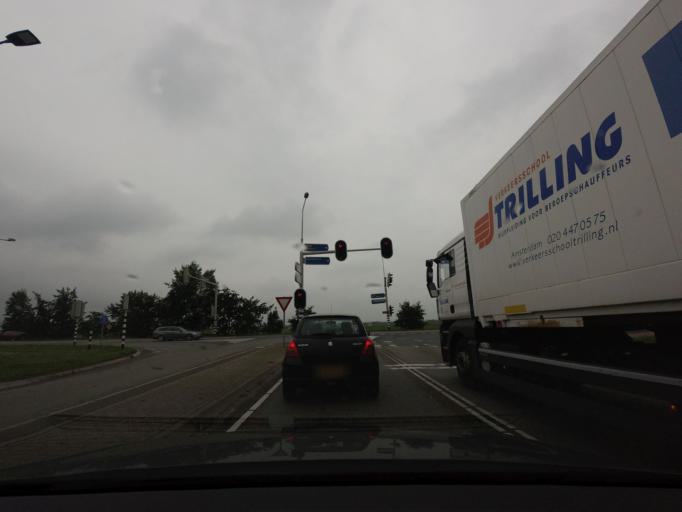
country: NL
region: North Holland
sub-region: Gemeente Aalsmeer
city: Aalsmeer
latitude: 52.3408
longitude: 4.7626
